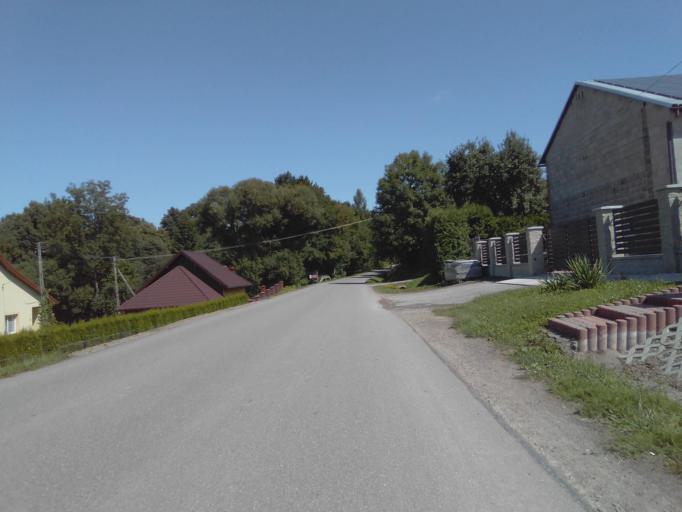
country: PL
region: Subcarpathian Voivodeship
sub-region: Powiat krosnienski
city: Jedlicze
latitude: 49.6708
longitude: 21.6111
